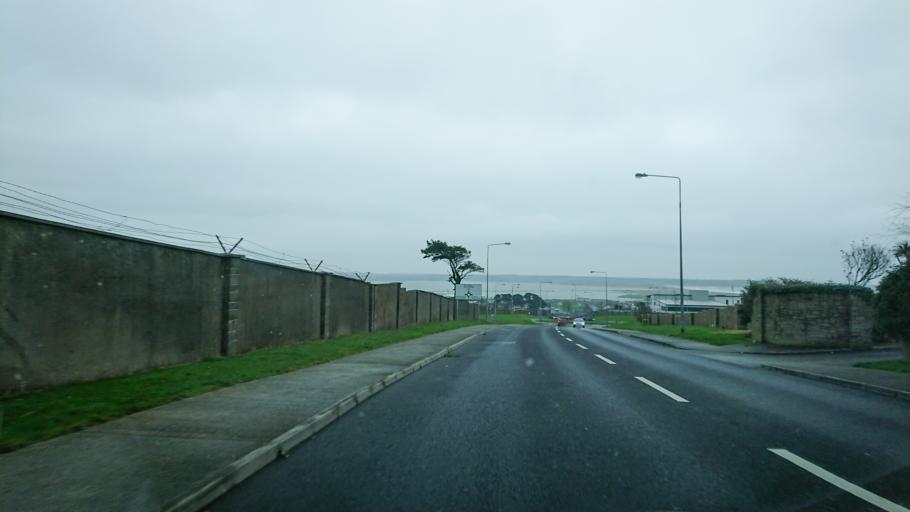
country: IE
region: Munster
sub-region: Waterford
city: Tra Mhor
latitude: 52.1704
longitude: -7.1496
